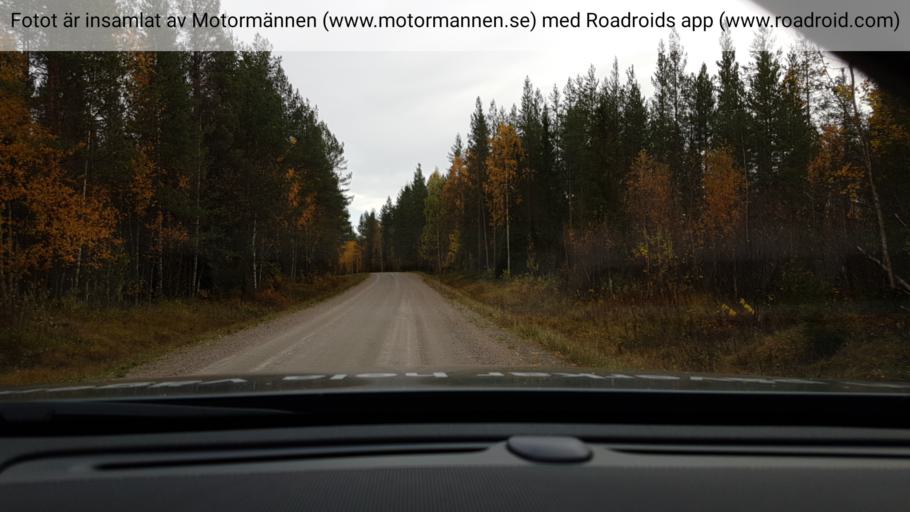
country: SE
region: Norrbotten
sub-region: Overkalix Kommun
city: OEverkalix
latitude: 66.2919
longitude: 22.9526
